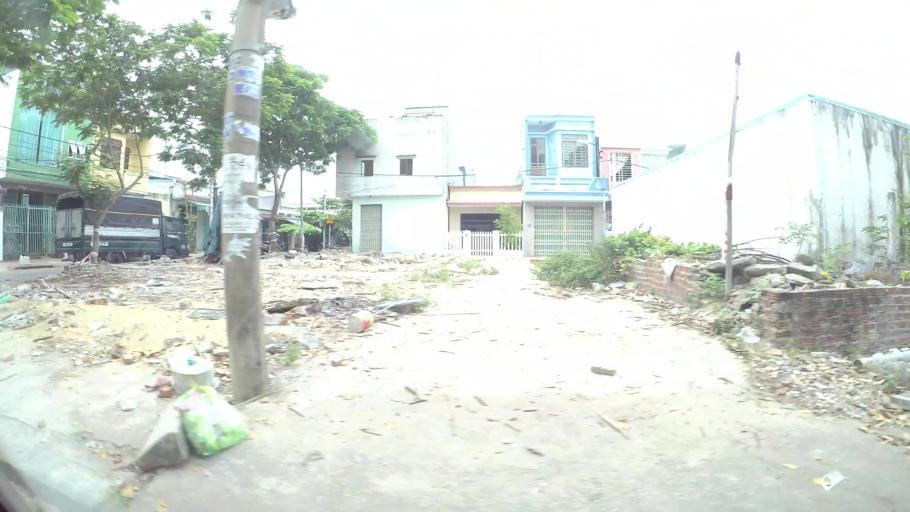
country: VN
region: Da Nang
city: Lien Chieu
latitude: 16.0747
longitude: 108.1731
